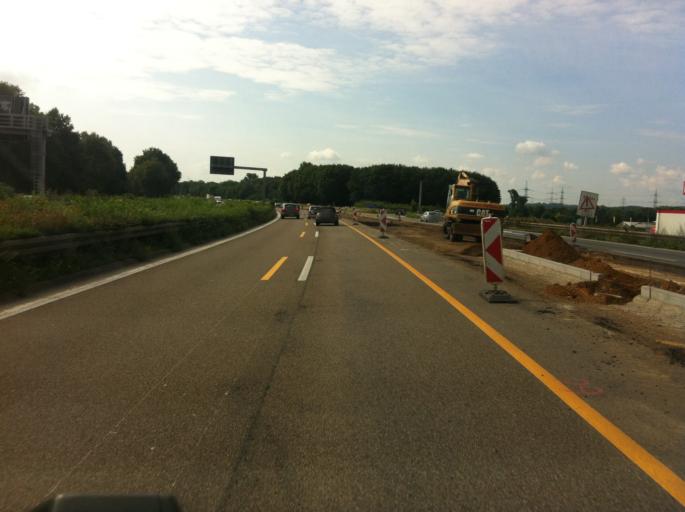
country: DE
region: North Rhine-Westphalia
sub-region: Regierungsbezirk Koln
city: Frechen
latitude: 50.9211
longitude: 6.8426
